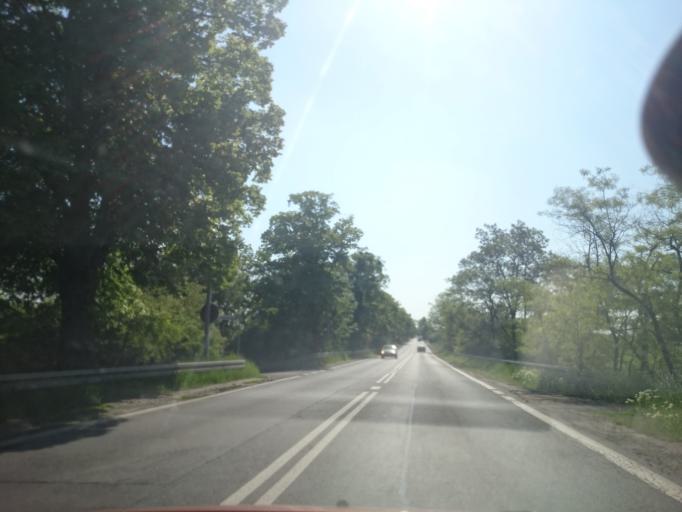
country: PL
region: Opole Voivodeship
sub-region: Powiat opolski
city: Opole
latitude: 50.6510
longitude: 17.9676
